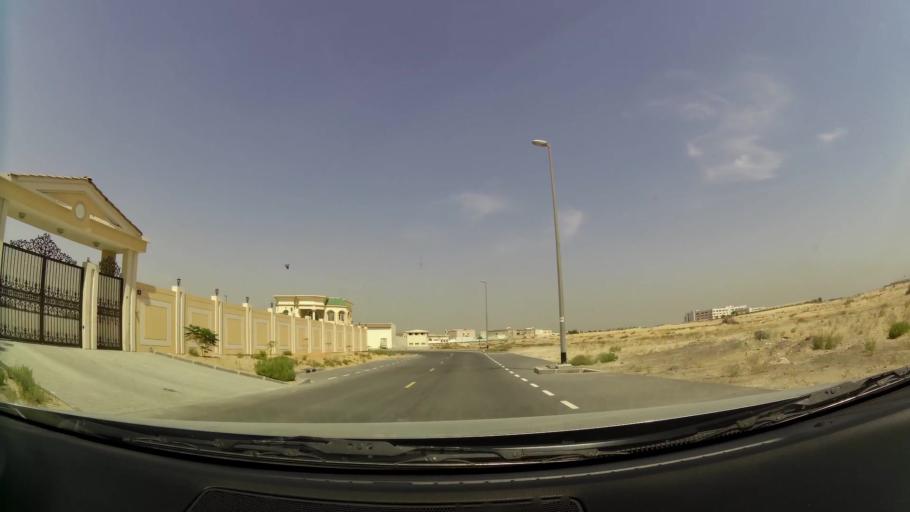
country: AE
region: Ash Shariqah
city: Sharjah
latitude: 25.1886
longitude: 55.4304
